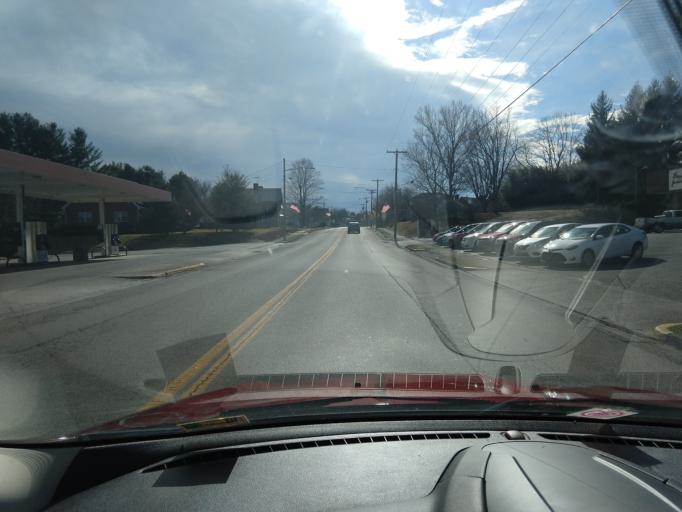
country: US
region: Virginia
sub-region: Floyd County
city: Floyd
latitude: 36.9147
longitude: -80.3124
